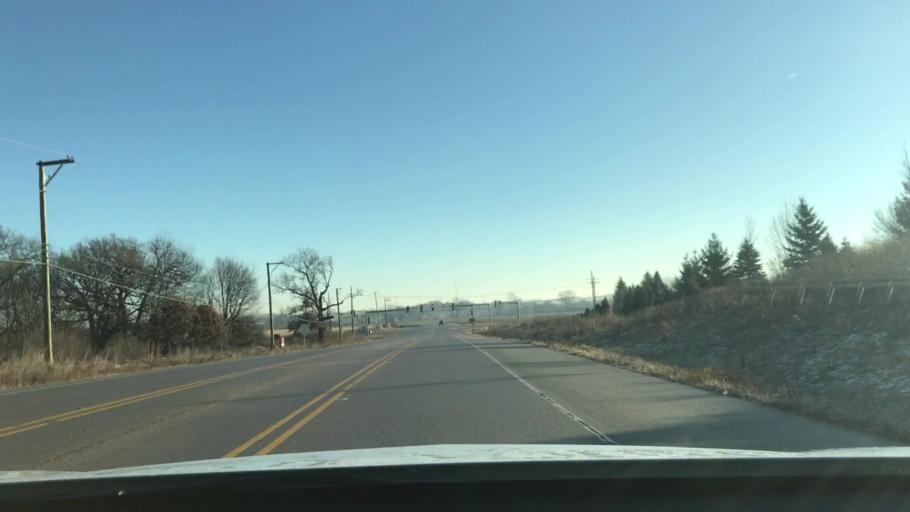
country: US
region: Illinois
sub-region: Kane County
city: Pingree Grove
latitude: 42.0976
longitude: -88.4054
